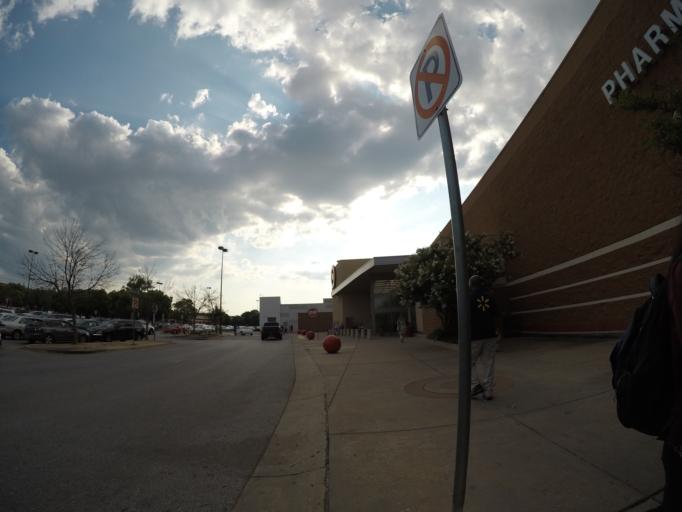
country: US
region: Maryland
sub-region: Prince George's County
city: University Park
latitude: 38.9680
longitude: -76.9551
